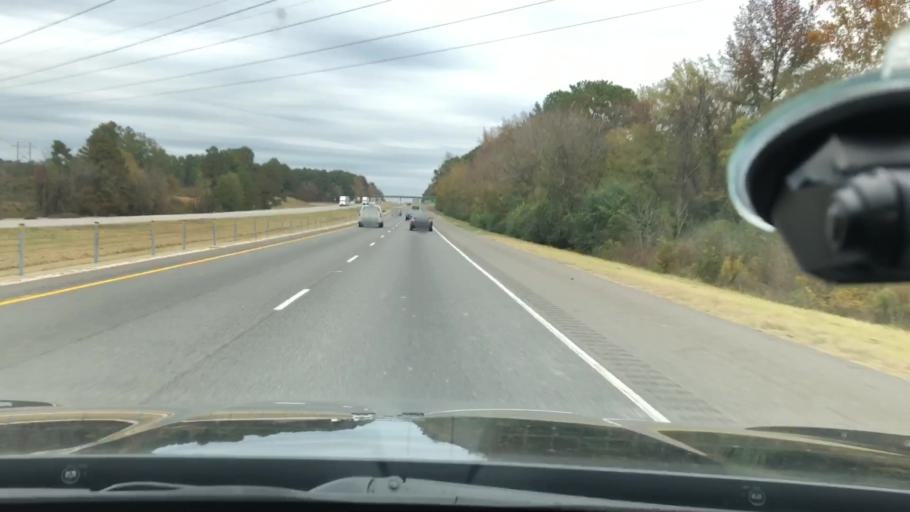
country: US
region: Arkansas
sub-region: Hot Spring County
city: Malvern
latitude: 34.3277
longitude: -92.9246
